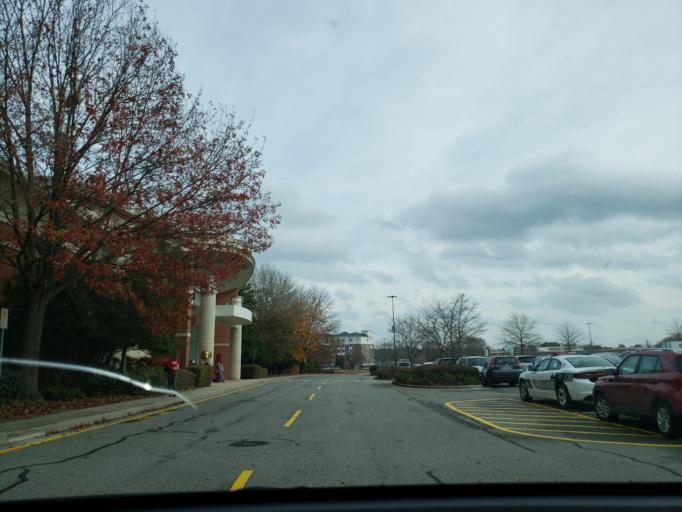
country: US
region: North Carolina
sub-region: Durham County
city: Durham
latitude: 35.9022
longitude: -78.9422
